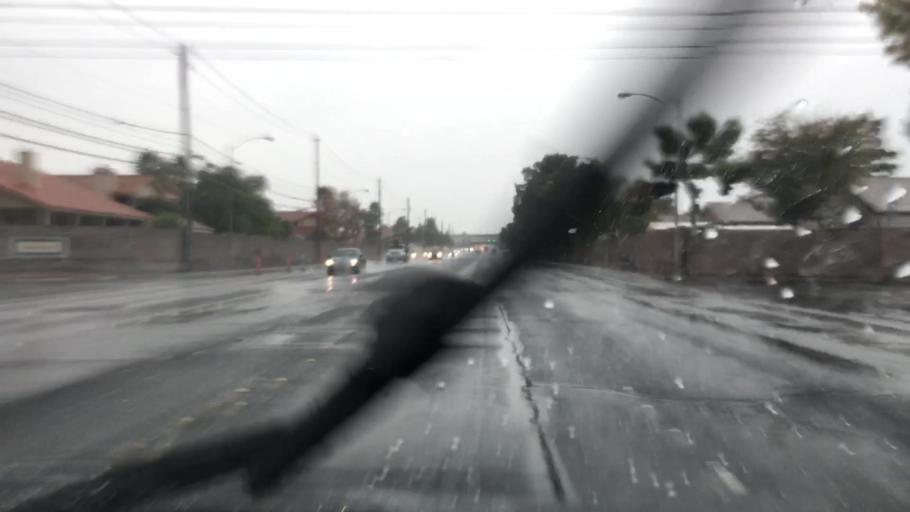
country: US
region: Nevada
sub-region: Clark County
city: Paradise
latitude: 36.0576
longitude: -115.1318
